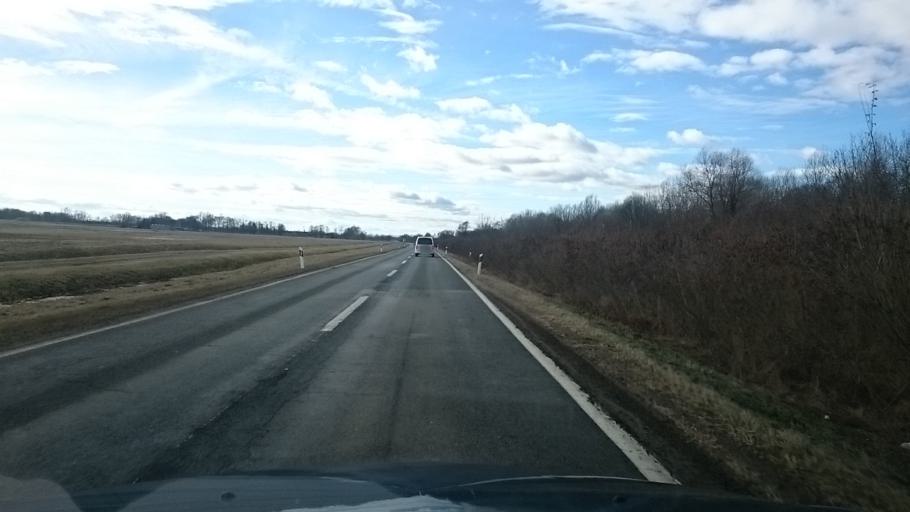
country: HR
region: Sisacko-Moslavacka
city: Novska
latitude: 45.2842
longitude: 16.9306
